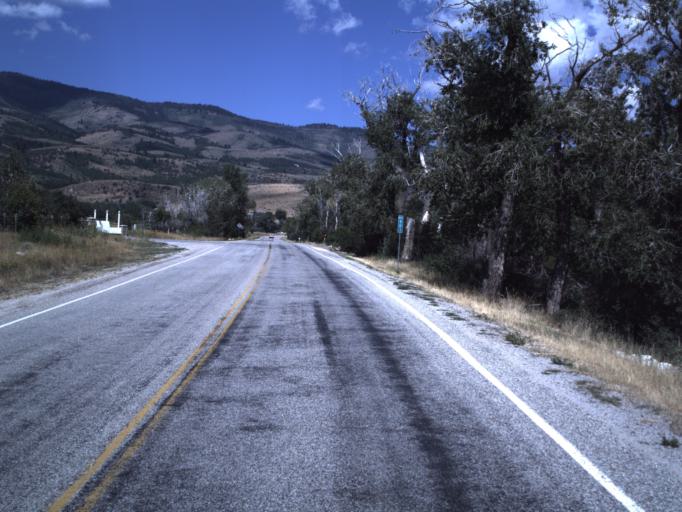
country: US
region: Idaho
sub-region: Bear Lake County
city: Paris
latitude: 41.9795
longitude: -111.4042
